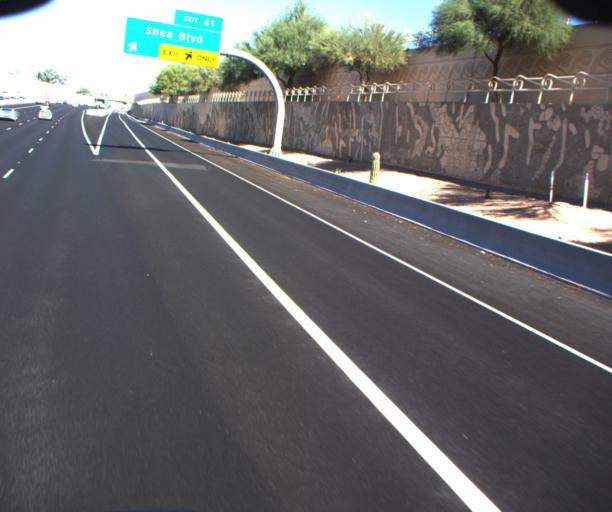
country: US
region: Arizona
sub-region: Maricopa County
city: Scottsdale
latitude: 33.5766
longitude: -111.8892
